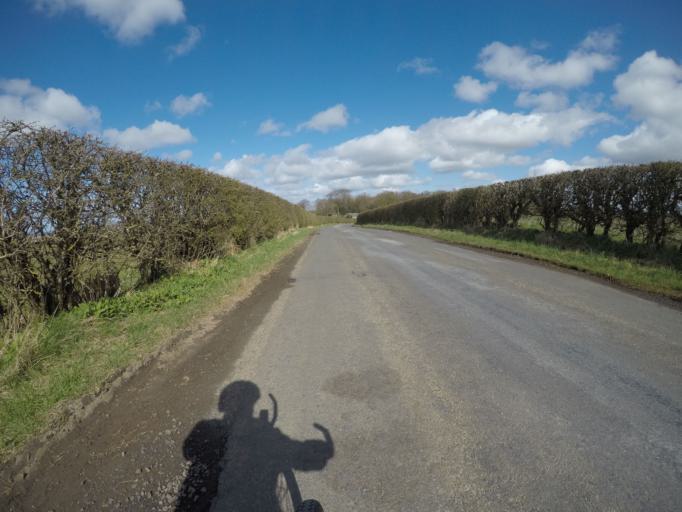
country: GB
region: Scotland
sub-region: North Ayrshire
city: Springside
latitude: 55.6092
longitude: -4.5759
